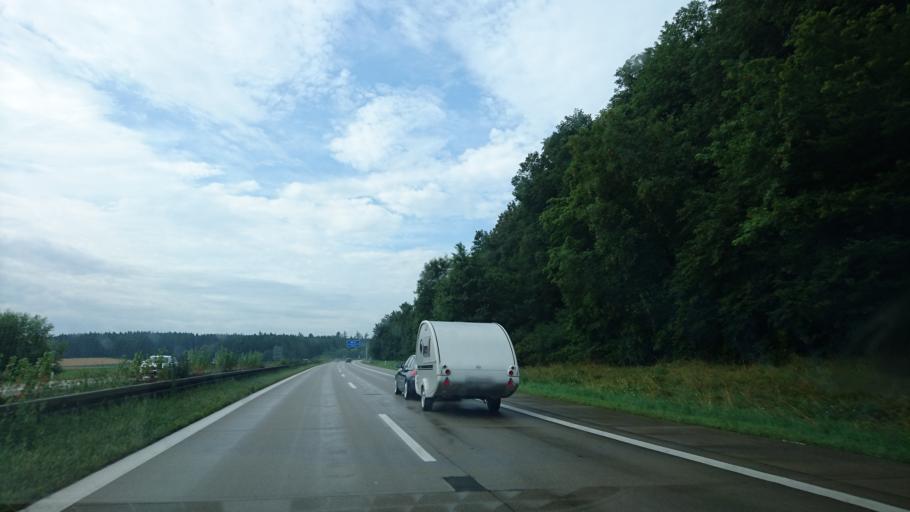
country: DE
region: Bavaria
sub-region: Lower Bavaria
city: Bad Abbach
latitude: 48.9145
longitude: 12.0878
